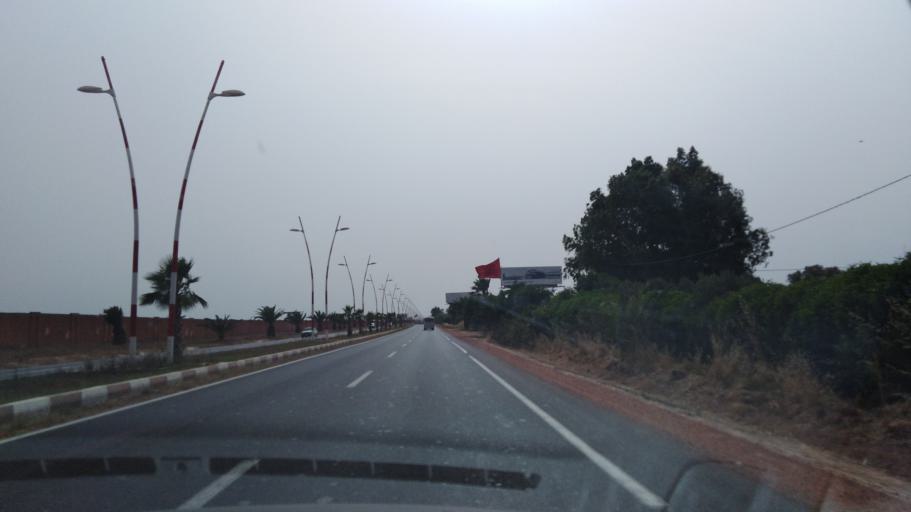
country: MA
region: Chaouia-Ouardigha
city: Nouaseur
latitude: 33.3943
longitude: -7.5964
